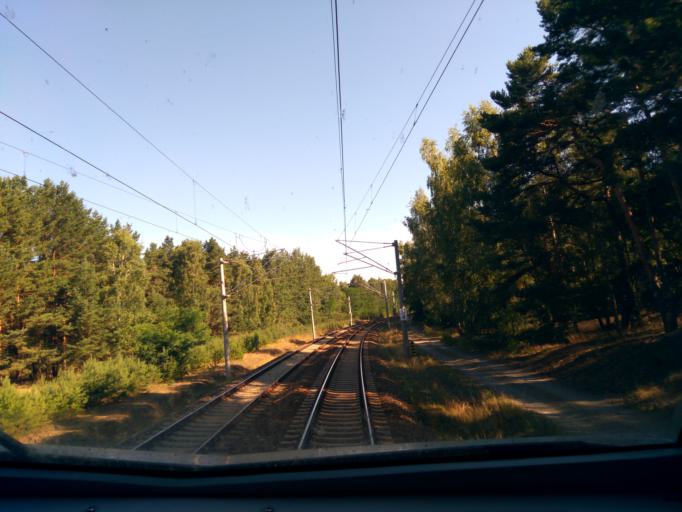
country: DE
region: Brandenburg
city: Bestensee
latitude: 52.2117
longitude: 13.6180
